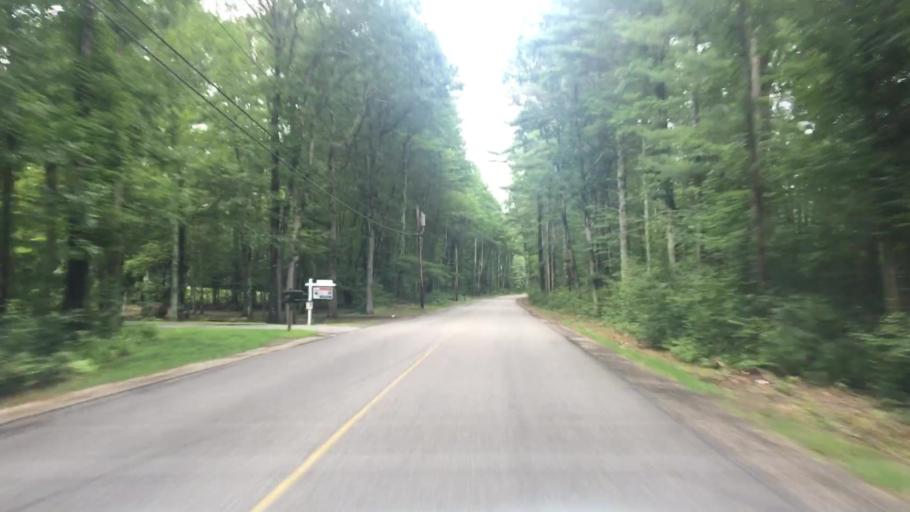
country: US
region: Maine
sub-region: York County
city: Dayton
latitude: 43.5305
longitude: -70.5856
